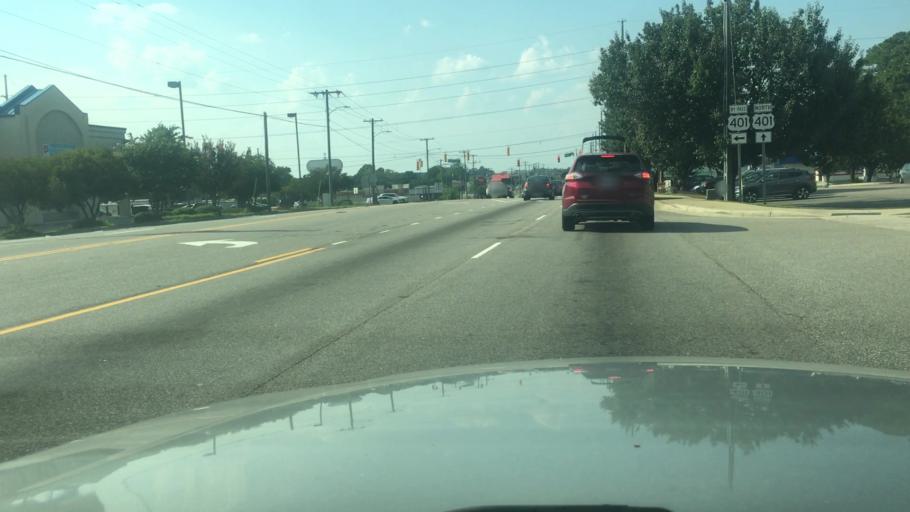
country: US
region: North Carolina
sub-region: Cumberland County
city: Fayetteville
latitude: 35.1040
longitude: -78.8782
